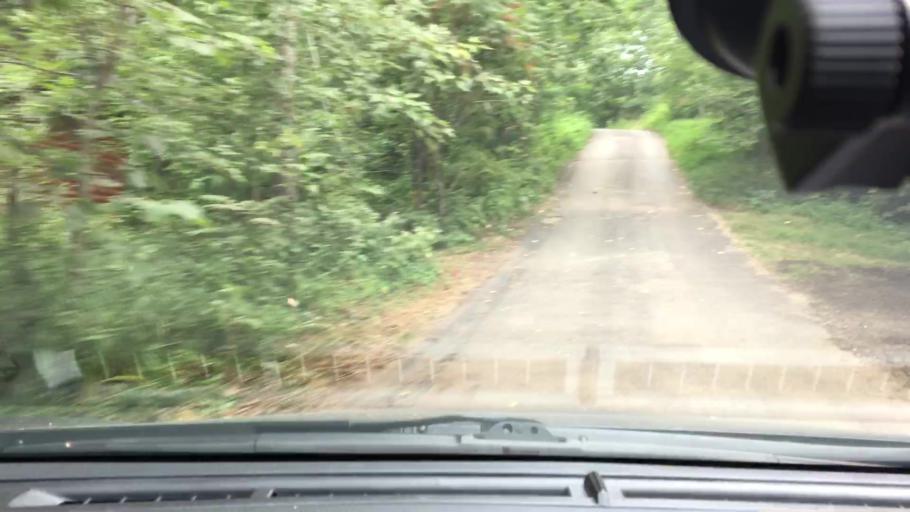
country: US
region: Minnesota
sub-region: Crow Wing County
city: Cross Lake
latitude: 46.8261
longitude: -93.9453
